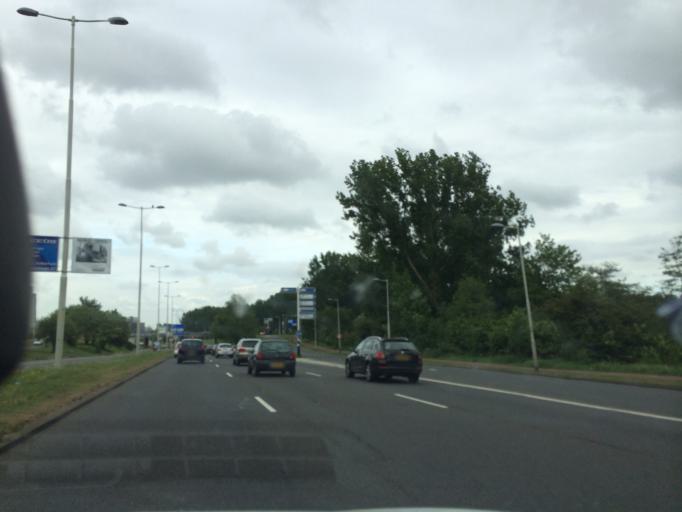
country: NL
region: South Holland
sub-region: Gemeente Rotterdam
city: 's-Gravenland
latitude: 51.9151
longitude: 4.5239
